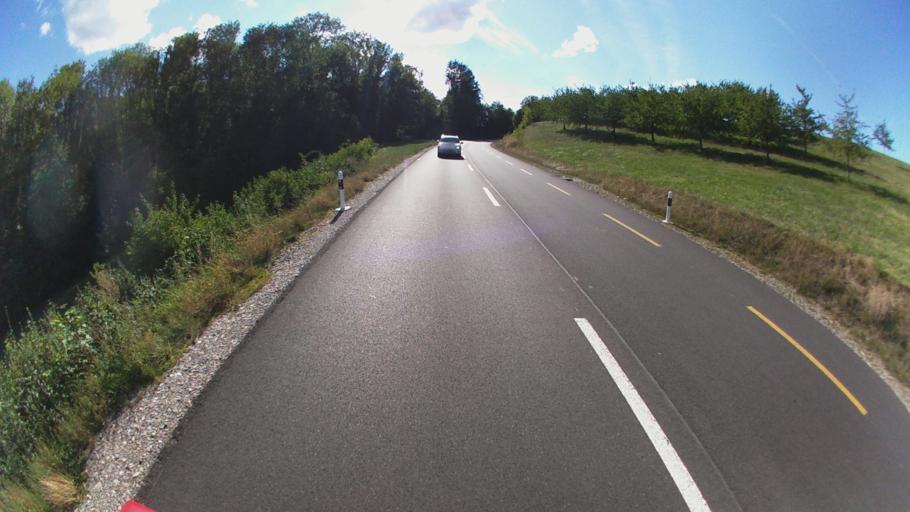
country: CH
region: Aargau
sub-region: Bezirk Rheinfelden
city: Wegenstetten
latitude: 47.5061
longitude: 7.9578
